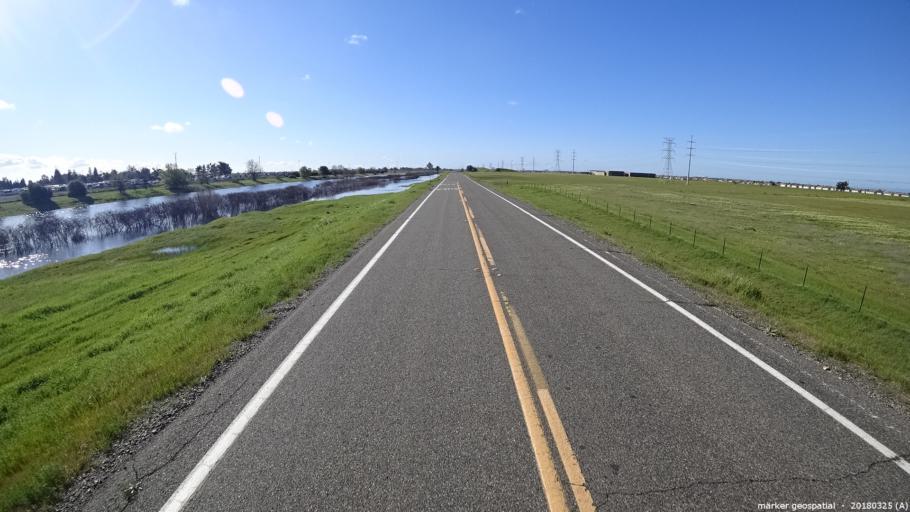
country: US
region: California
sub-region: Sacramento County
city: Elverta
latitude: 38.6842
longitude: -121.4855
